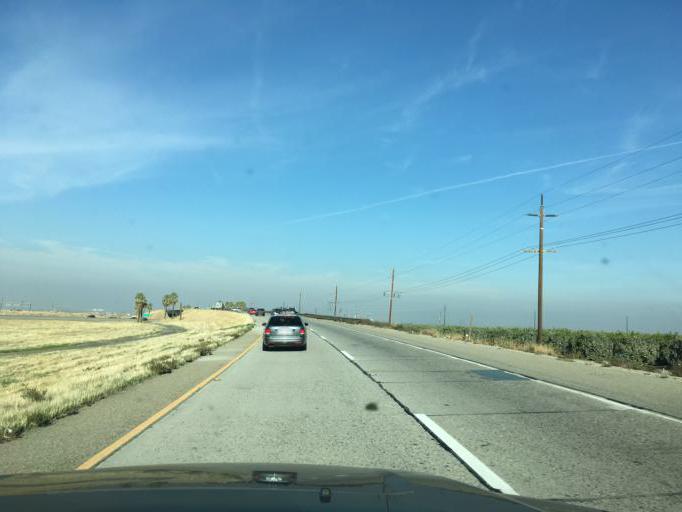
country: US
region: California
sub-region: Kern County
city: Frazier Park
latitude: 35.0154
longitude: -118.9527
